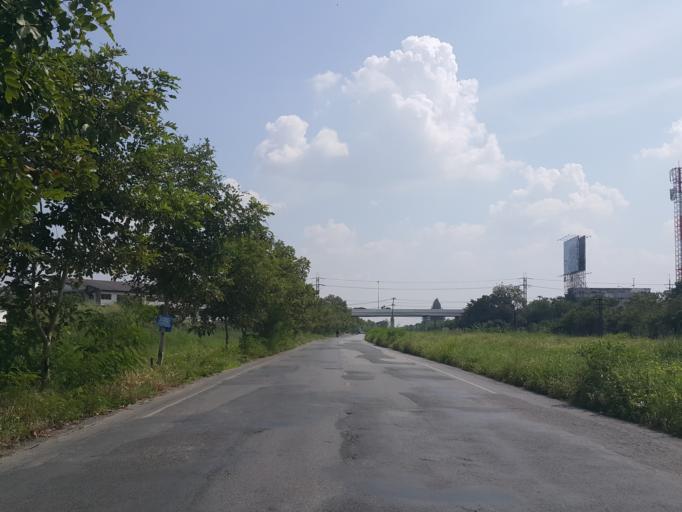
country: TH
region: Chiang Mai
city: Chiang Mai
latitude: 18.7634
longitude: 99.0191
